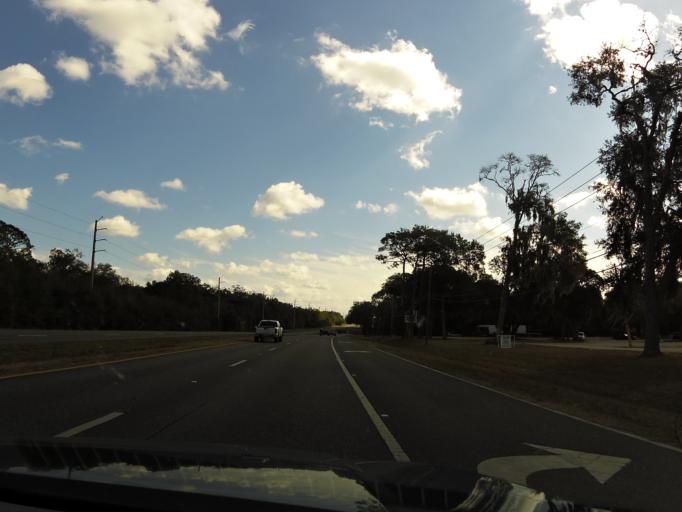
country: US
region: Florida
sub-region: Volusia County
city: North DeLand
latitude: 29.0860
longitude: -81.3223
